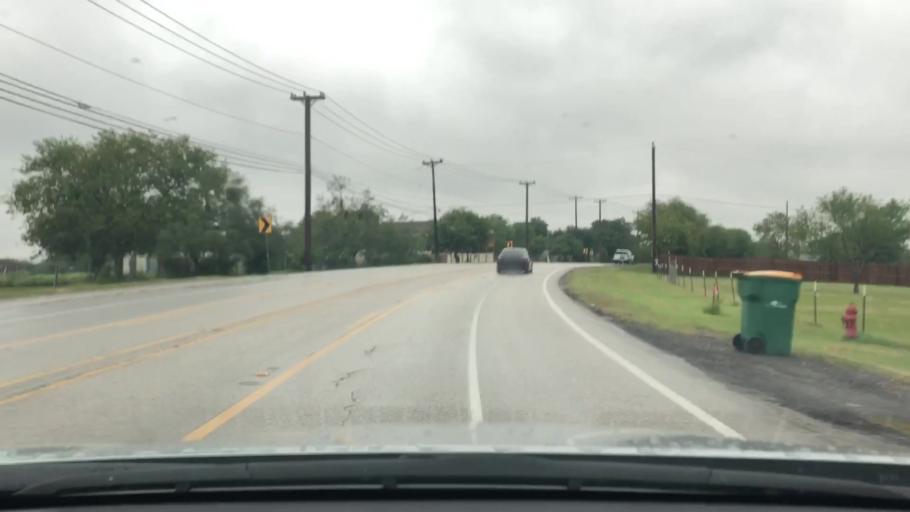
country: US
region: Texas
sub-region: Bexar County
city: Converse
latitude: 29.4928
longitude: -98.3111
